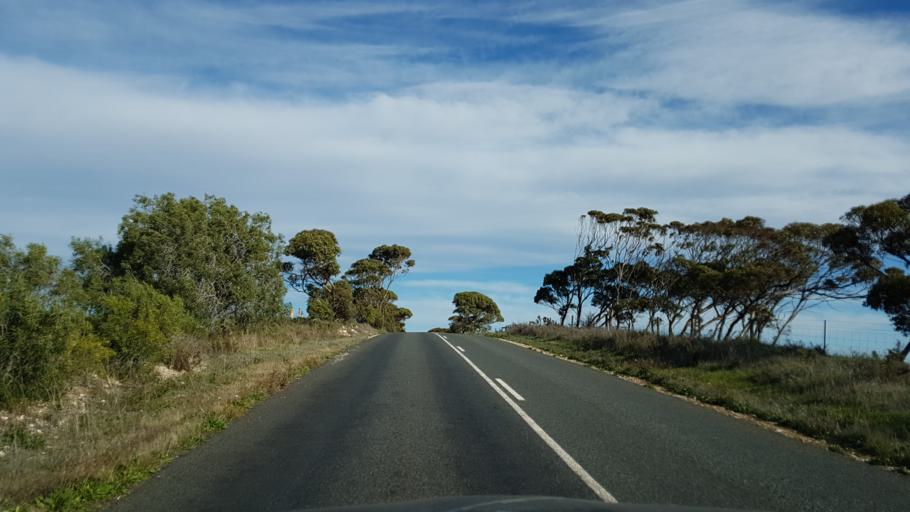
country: AU
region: South Australia
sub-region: Murray Bridge
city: Tailem Bend
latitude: -35.1832
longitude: 139.4612
